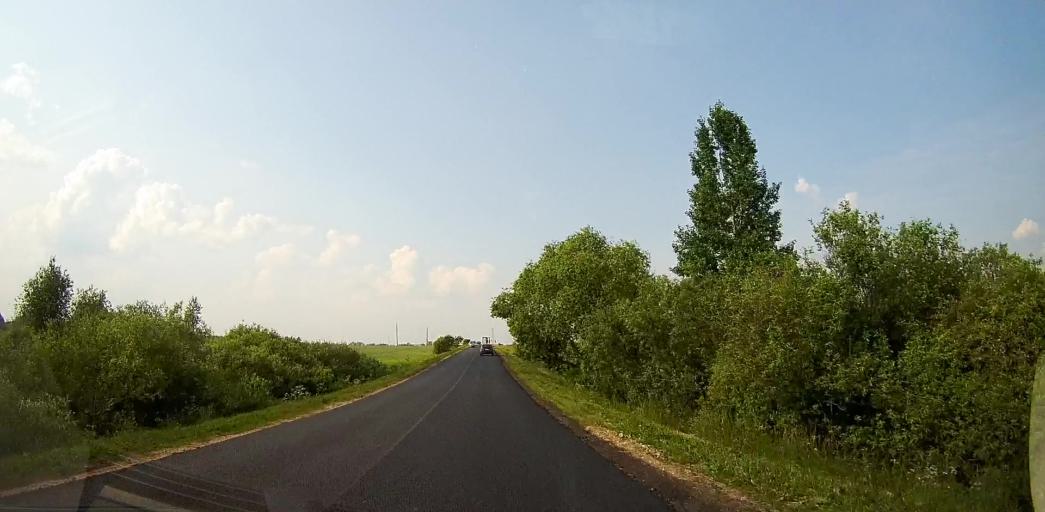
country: RU
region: Moskovskaya
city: Barybino
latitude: 55.2414
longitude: 37.9178
